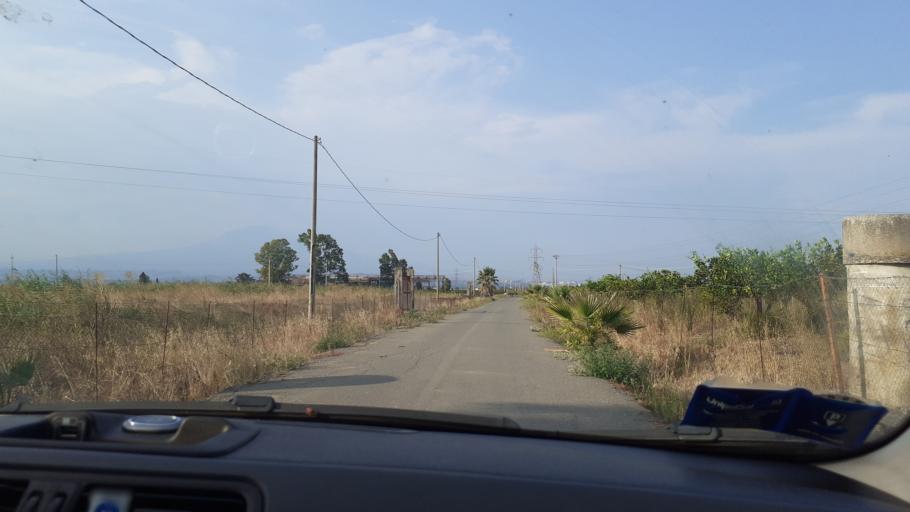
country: IT
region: Sicily
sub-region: Catania
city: Catania
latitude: 37.4211
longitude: 15.0079
